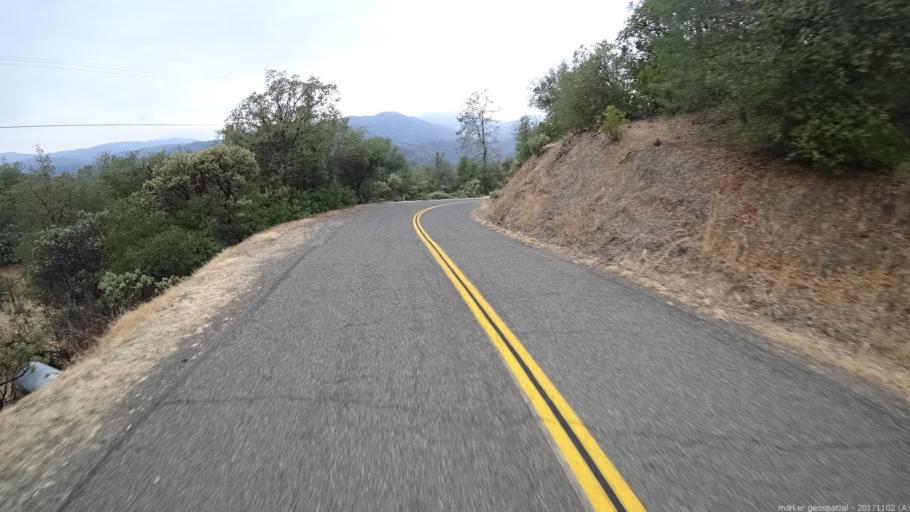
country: US
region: California
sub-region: Shasta County
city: Central Valley (historical)
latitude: 40.6573
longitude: -122.4271
